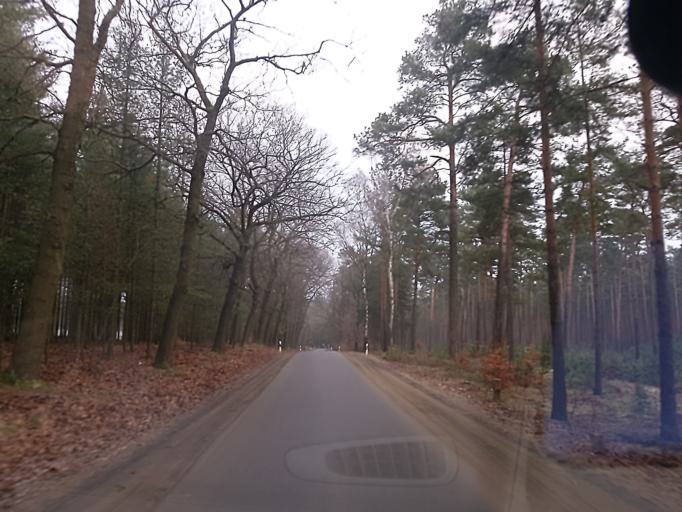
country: DE
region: Brandenburg
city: Crinitz
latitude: 51.7072
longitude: 13.7808
